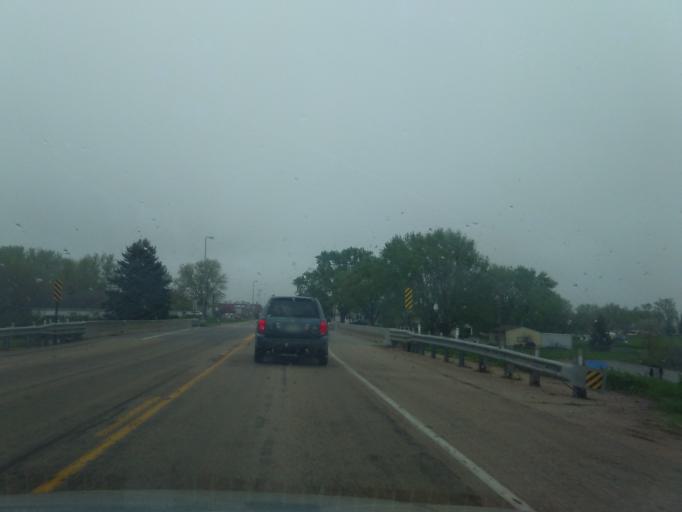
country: US
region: Nebraska
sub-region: Wayne County
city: Wayne
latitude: 42.2239
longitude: -97.0178
